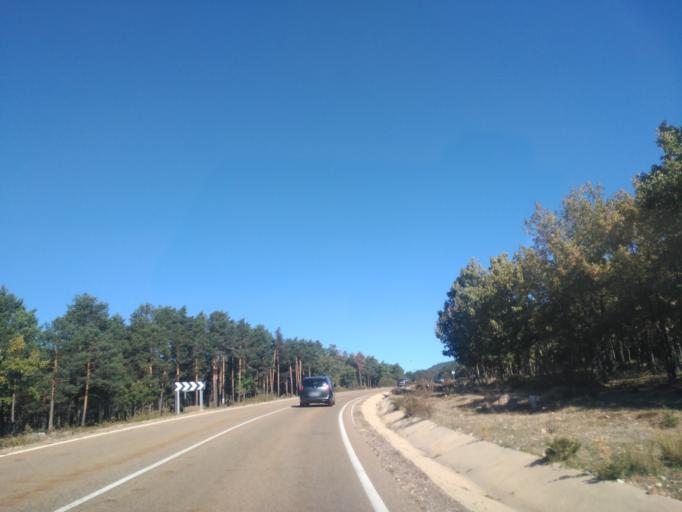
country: ES
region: Castille and Leon
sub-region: Provincia de Soria
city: Vinuesa
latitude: 41.9449
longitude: -2.7730
